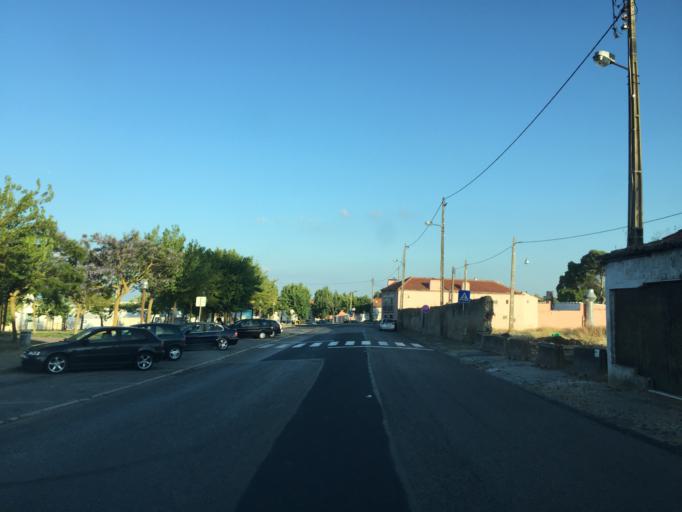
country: PT
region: Lisbon
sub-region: Odivelas
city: Olival do Basto
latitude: 38.7861
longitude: -9.1438
